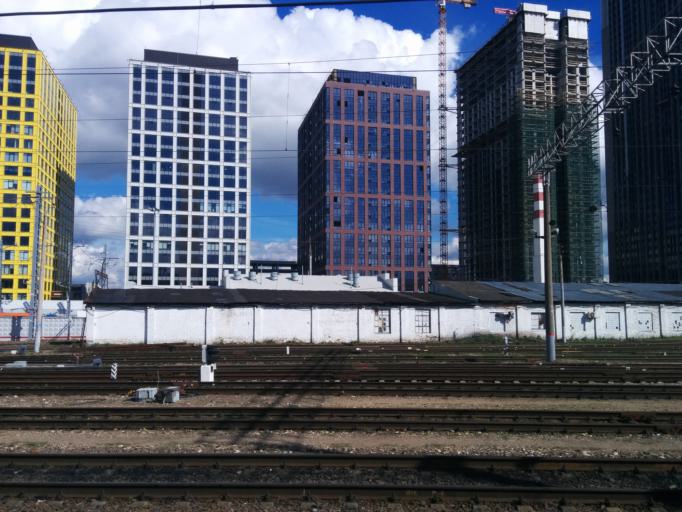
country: RU
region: Moscow
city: Mar'ina Roshcha
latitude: 55.8037
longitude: 37.5876
